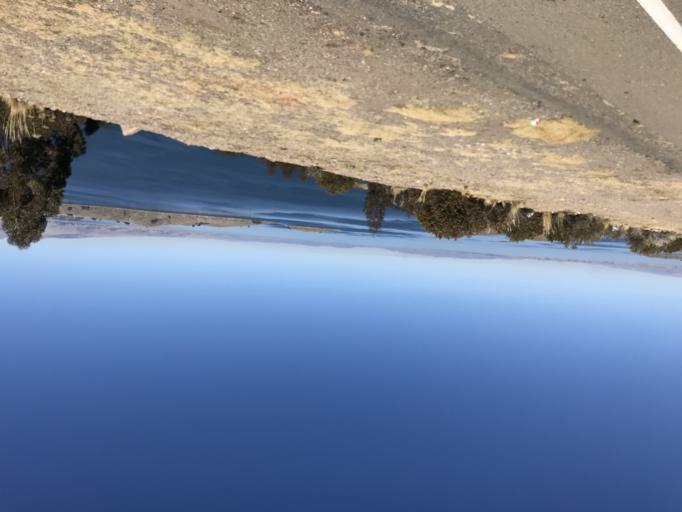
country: BO
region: La Paz
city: San Pedro
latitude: -16.1953
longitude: -68.9140
